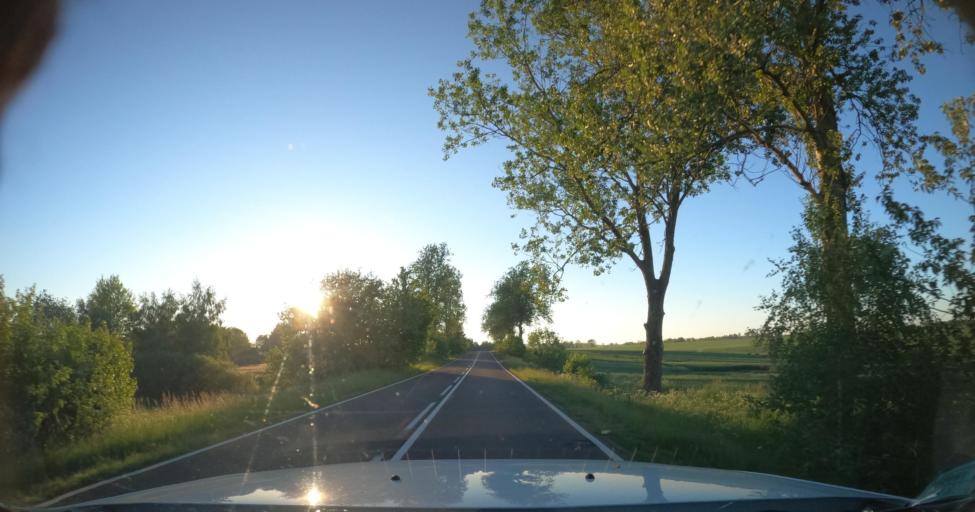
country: PL
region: Pomeranian Voivodeship
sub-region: Powiat slupski
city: Damnica
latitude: 54.4303
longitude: 17.3628
